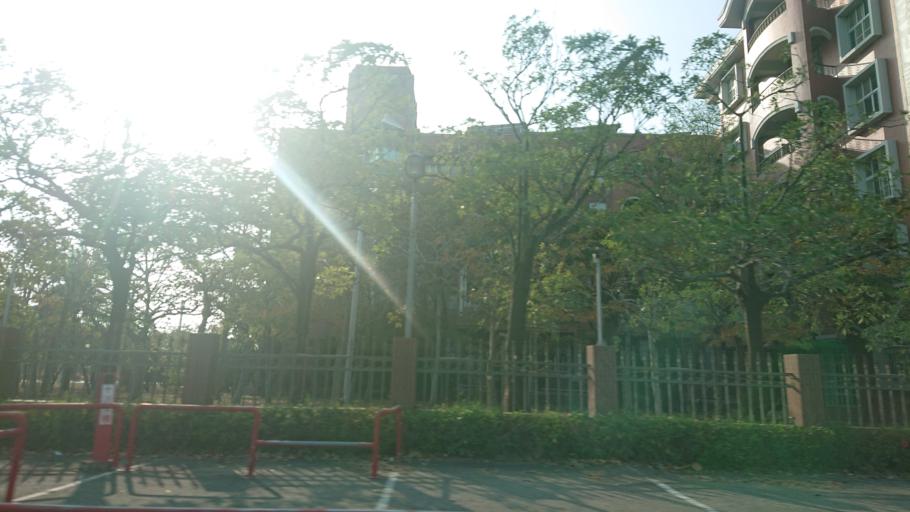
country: TW
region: Taiwan
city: Xinying
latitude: 23.1913
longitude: 120.2713
